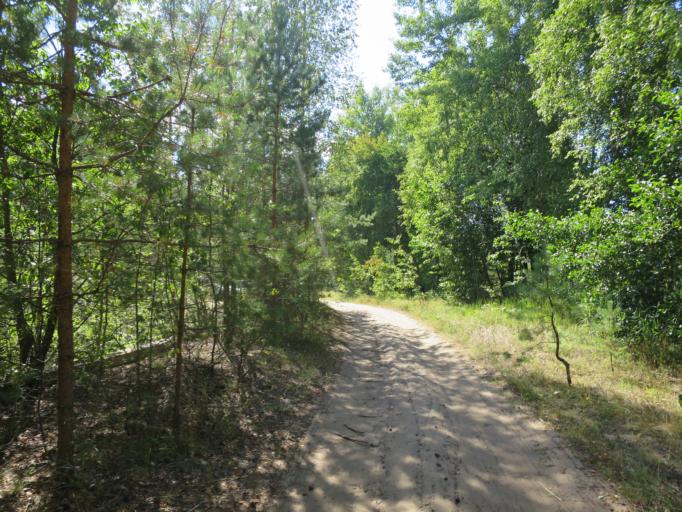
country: LV
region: Adazi
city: Adazi
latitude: 57.1119
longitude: 24.3569
